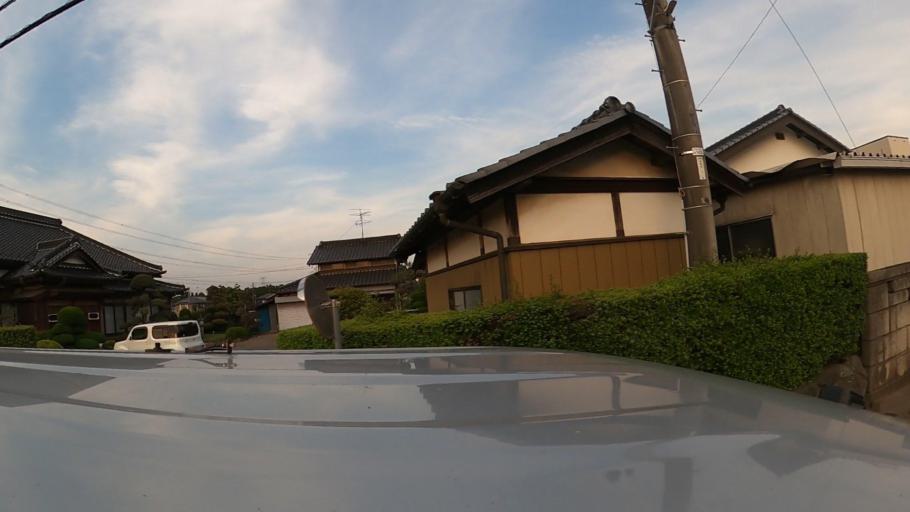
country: JP
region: Ibaraki
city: Ushiku
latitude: 36.0011
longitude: 140.1243
